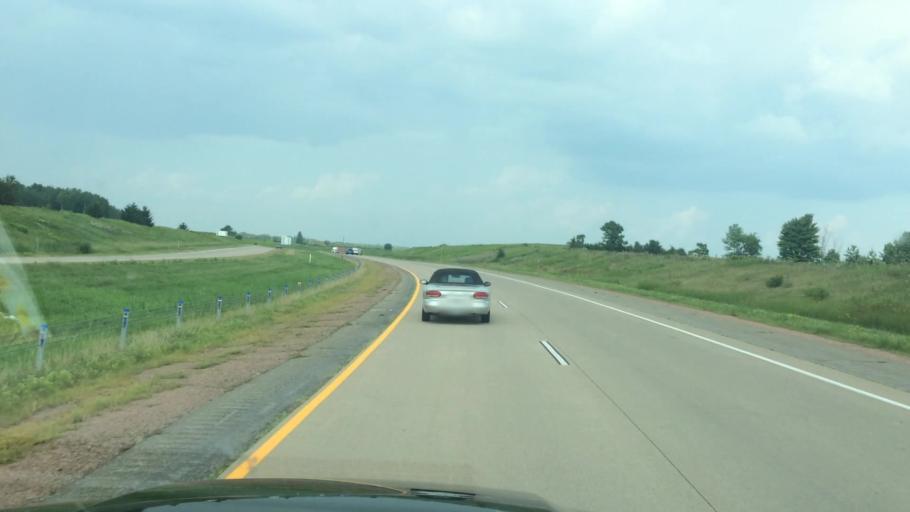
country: US
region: Wisconsin
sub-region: Clark County
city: Abbotsford
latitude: 44.9363
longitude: -90.2938
